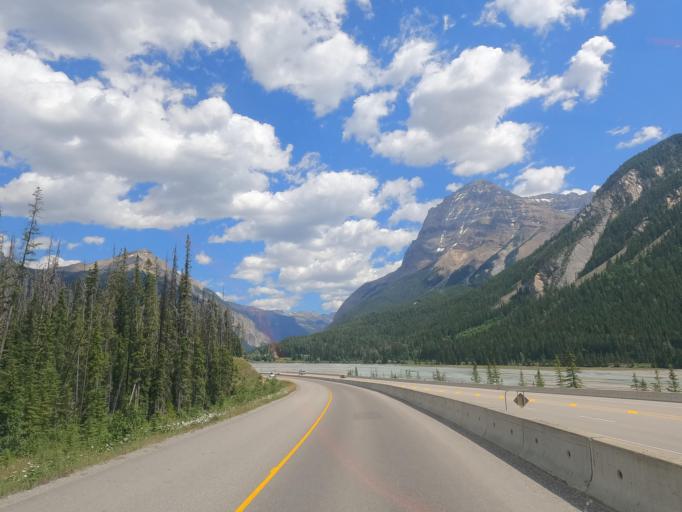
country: CA
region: Alberta
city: Lake Louise
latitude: 51.3834
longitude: -116.5071
